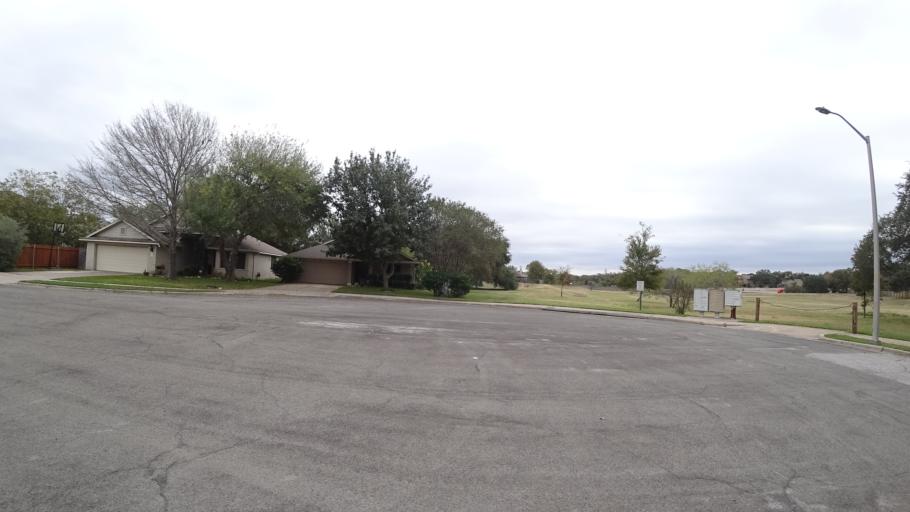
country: US
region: Texas
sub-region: Travis County
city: Shady Hollow
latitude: 30.1513
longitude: -97.8523
